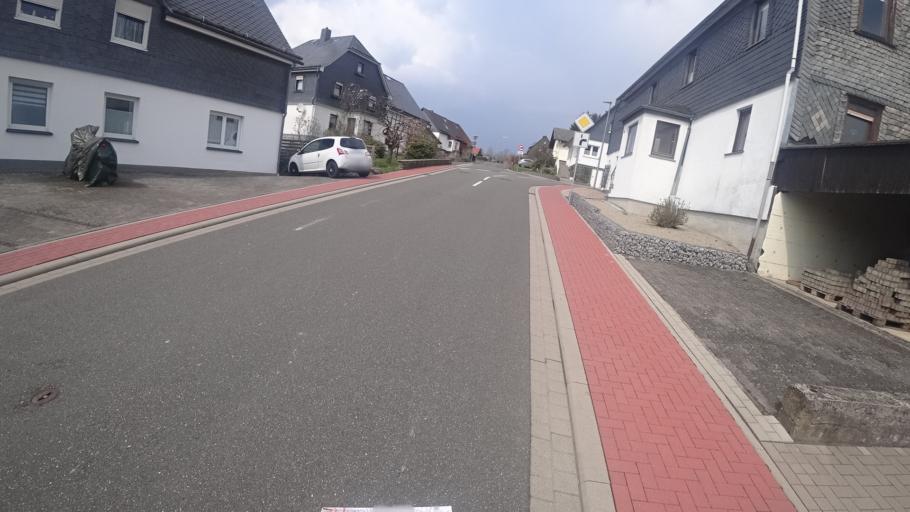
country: DE
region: Rheinland-Pfalz
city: Luckenbach
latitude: 50.7132
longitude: 7.8468
